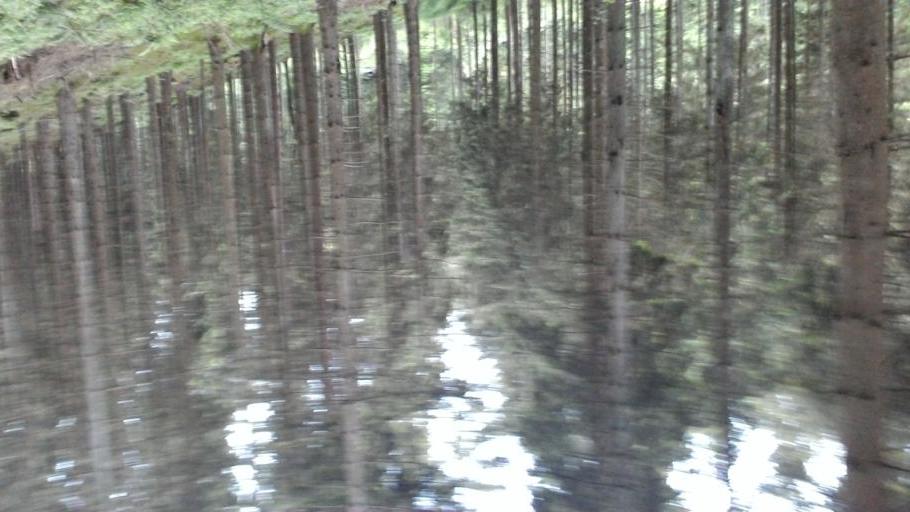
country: DE
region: North Rhine-Westphalia
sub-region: Regierungsbezirk Koln
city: Monschau
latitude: 50.5457
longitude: 6.2081
